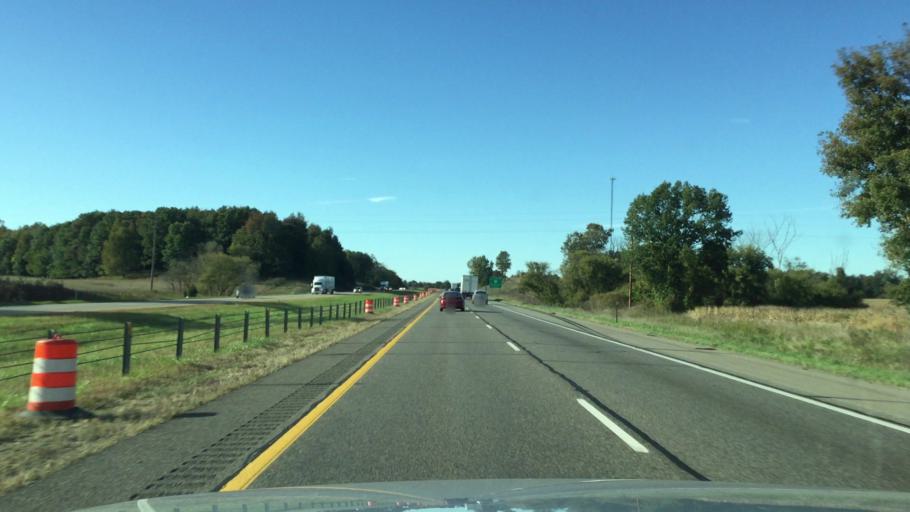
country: US
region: Michigan
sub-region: Calhoun County
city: Albion
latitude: 42.2721
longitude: -84.7805
